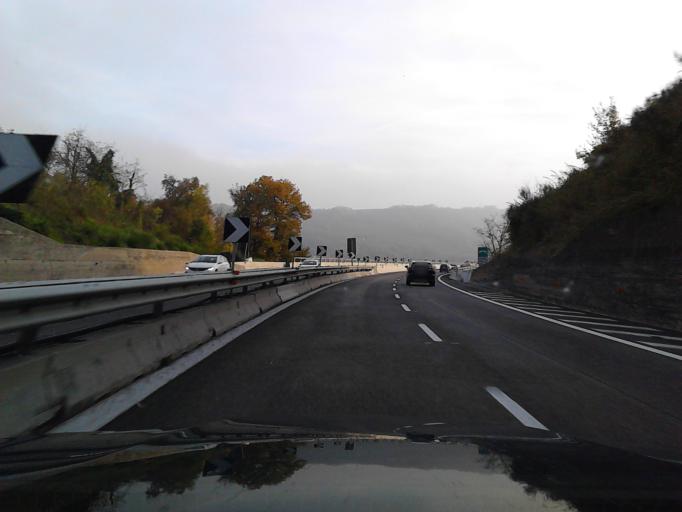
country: IT
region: Abruzzo
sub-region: Provincia di Chieti
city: San Vito Chietino
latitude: 42.2968
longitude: 14.4324
